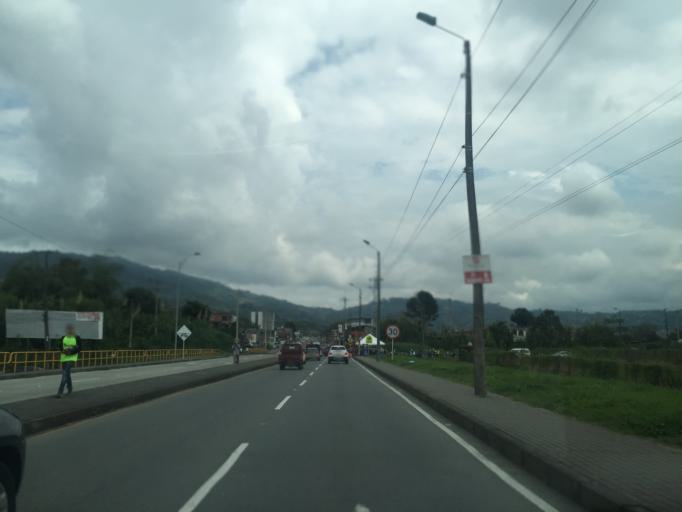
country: CO
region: Risaralda
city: Dos Quebradas
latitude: 4.8388
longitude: -75.6753
